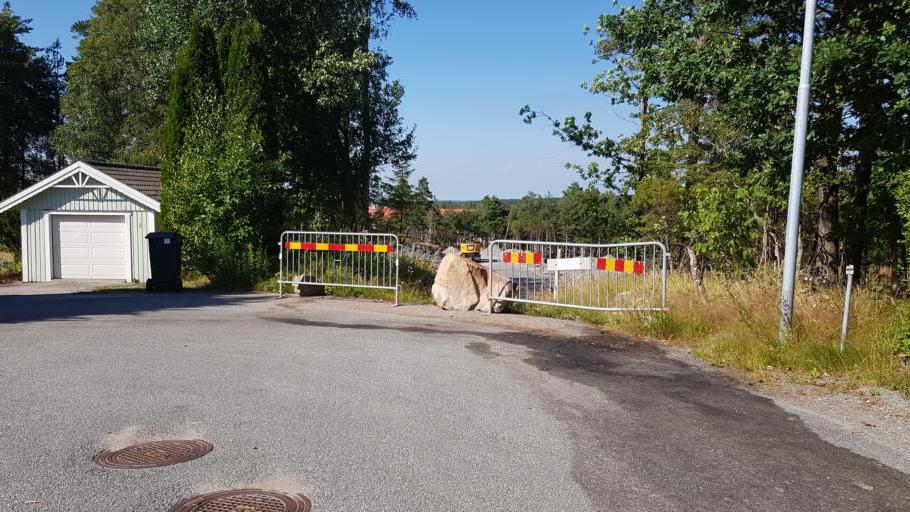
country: SE
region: Vaestra Goetaland
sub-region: Partille Kommun
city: Furulund
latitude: 57.6973
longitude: 12.1448
